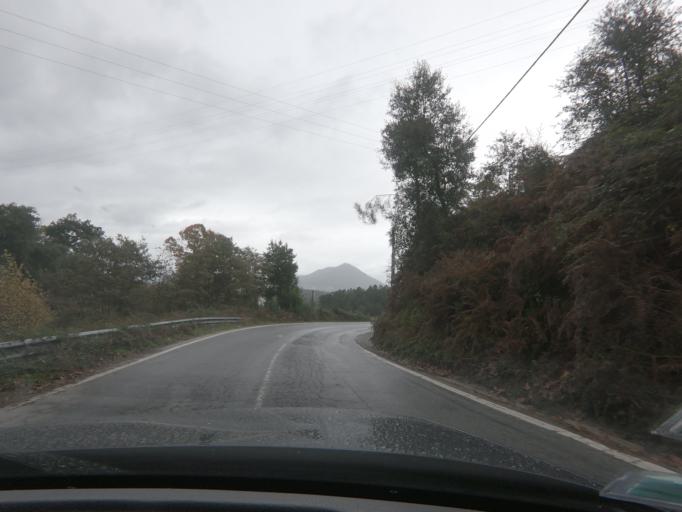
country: PT
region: Braga
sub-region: Celorico de Basto
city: Celorico de Basto
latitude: 41.4177
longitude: -7.9924
